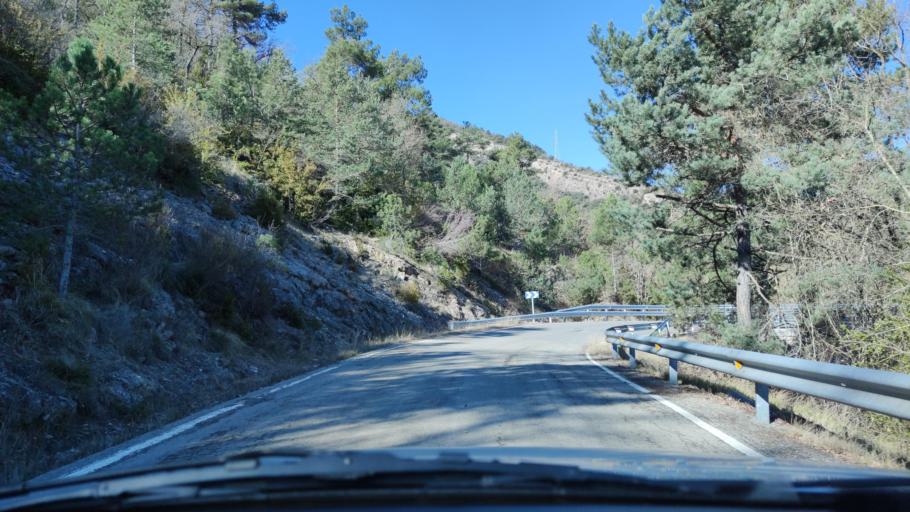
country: ES
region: Catalonia
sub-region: Provincia de Lleida
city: Llimiana
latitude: 42.0444
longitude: 1.0379
